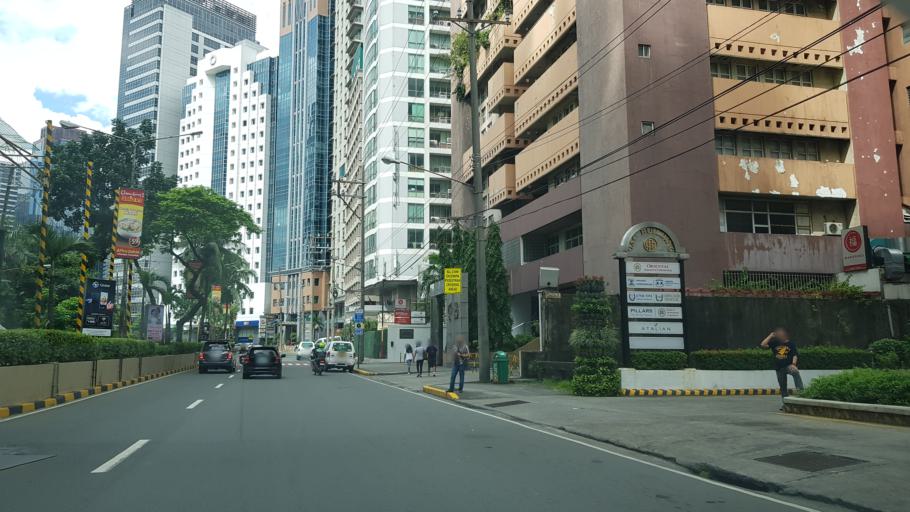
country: PH
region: Metro Manila
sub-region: Pasig
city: Pasig City
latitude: 14.5806
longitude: 121.0593
